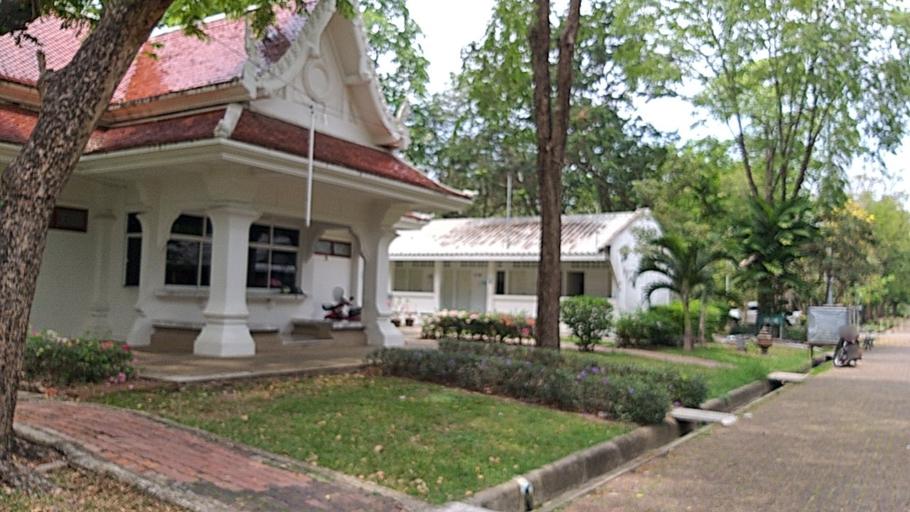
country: TH
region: Bangkok
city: Thawi Watthana
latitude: 13.7780
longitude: 100.3202
